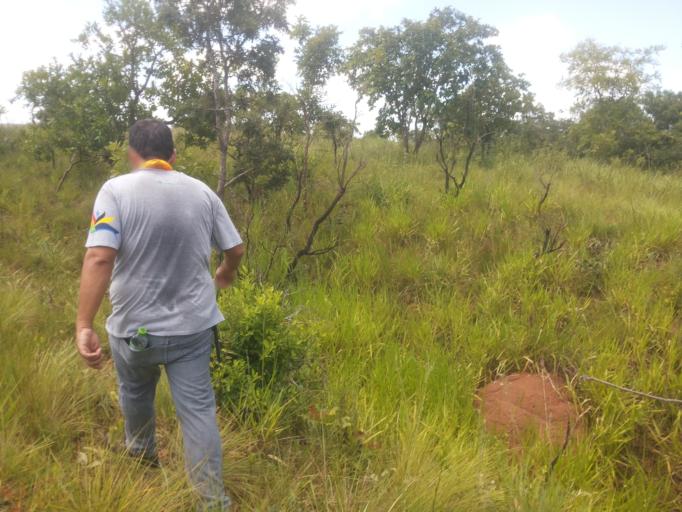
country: BR
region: Minas Gerais
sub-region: Ituiutaba
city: Ituiutaba
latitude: -19.0331
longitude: -49.4685
